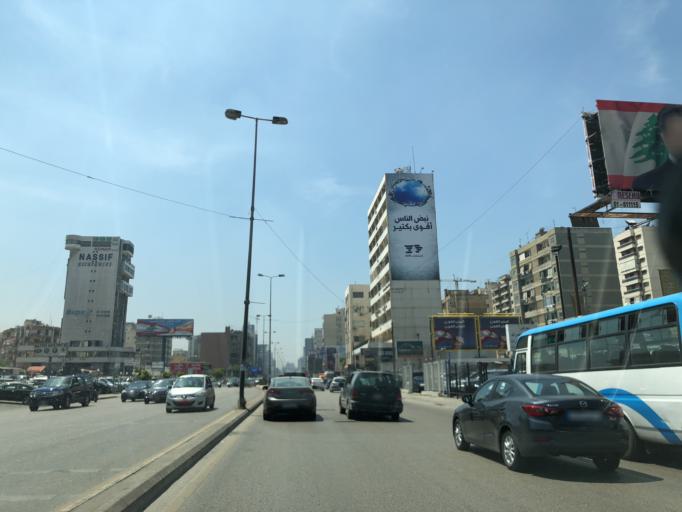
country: LB
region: Mont-Liban
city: Jdaidet el Matn
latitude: 33.8919
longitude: 35.5581
